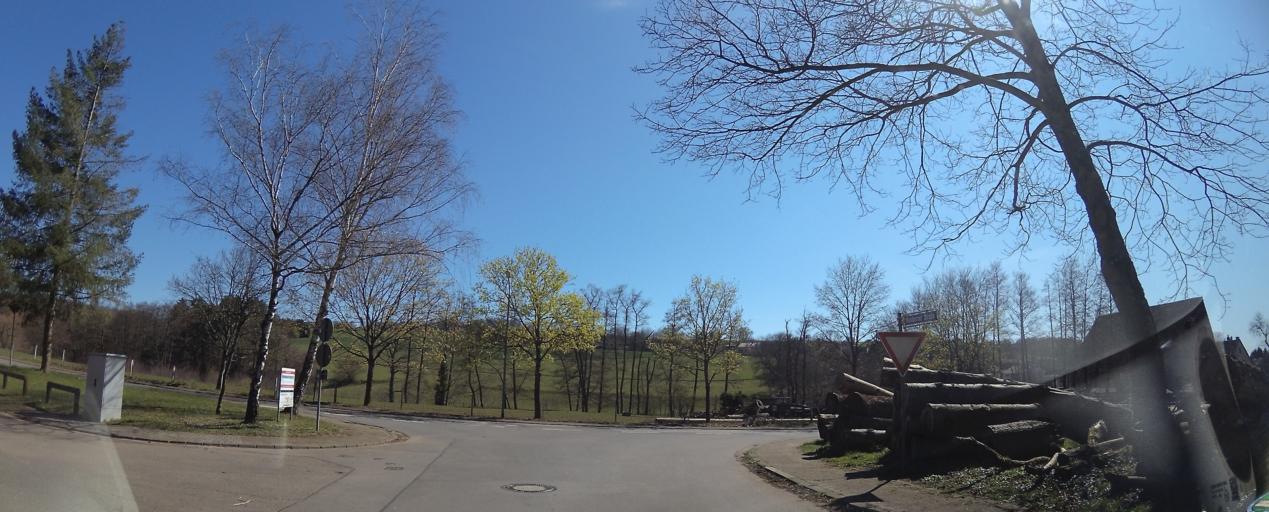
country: DE
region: Saarland
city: Heusweiler
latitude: 49.3411
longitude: 6.9646
